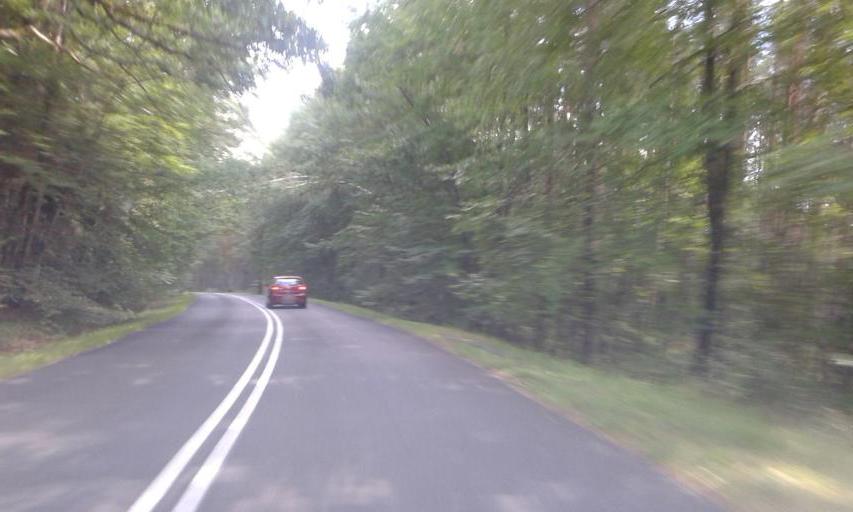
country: PL
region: West Pomeranian Voivodeship
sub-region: Powiat koszalinski
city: Polanow
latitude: 54.2369
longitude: 16.7078
